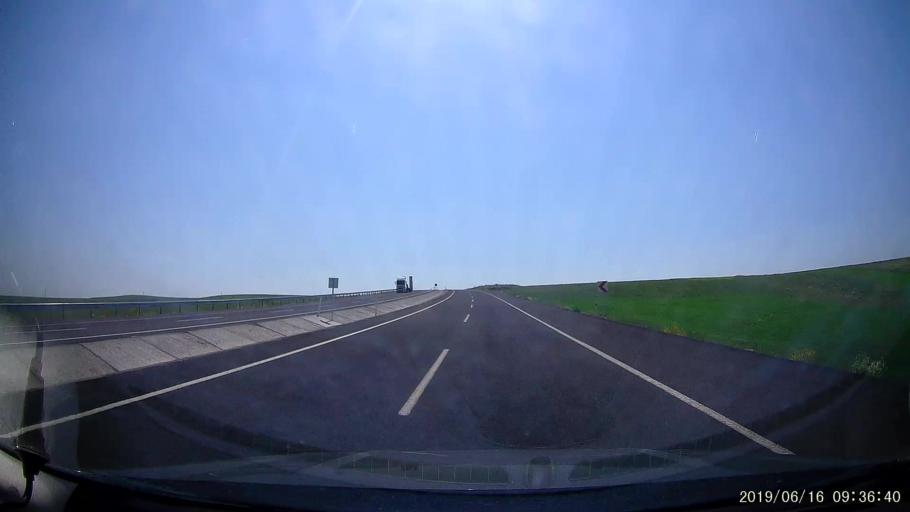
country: TR
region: Kars
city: Kars
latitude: 40.5563
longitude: 43.1772
